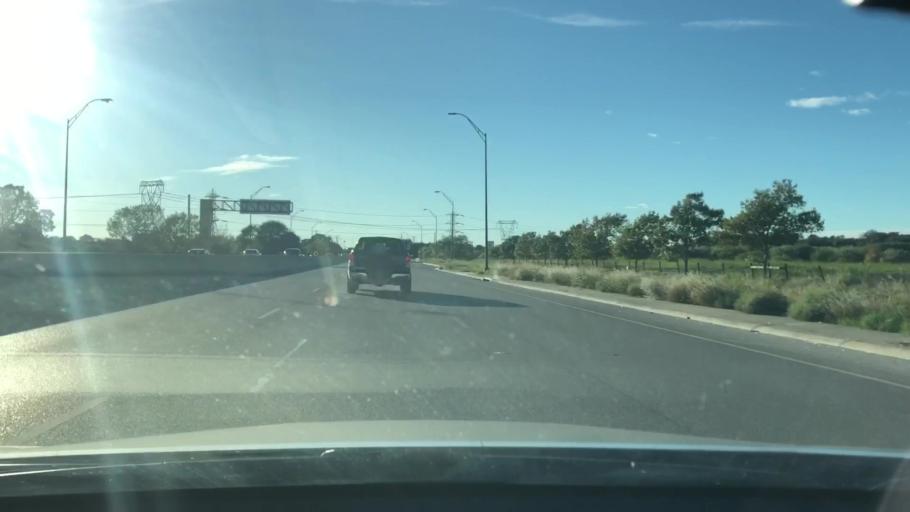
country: US
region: Texas
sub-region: Bexar County
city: Alamo Heights
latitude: 29.5470
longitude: -98.4434
